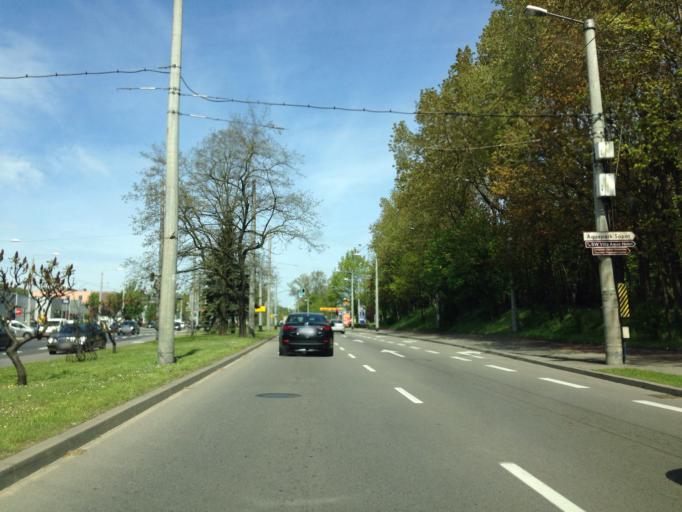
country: PL
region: Pomeranian Voivodeship
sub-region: Sopot
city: Sopot
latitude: 54.4575
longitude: 18.5555
